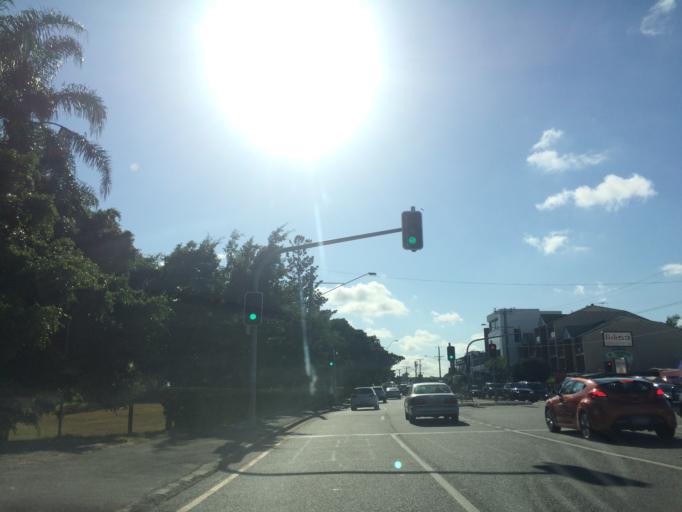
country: AU
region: Queensland
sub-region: Brisbane
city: Woolloongabba
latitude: -27.4790
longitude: 153.0434
